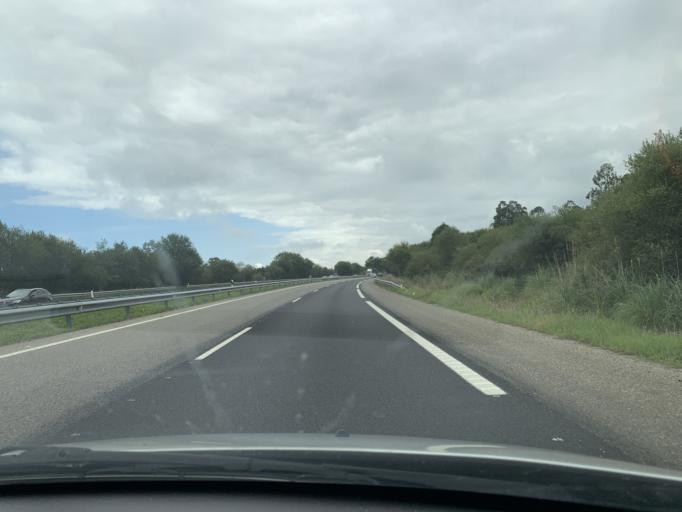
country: ES
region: Asturias
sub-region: Province of Asturias
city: Llanes
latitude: 43.4224
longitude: -4.8010
